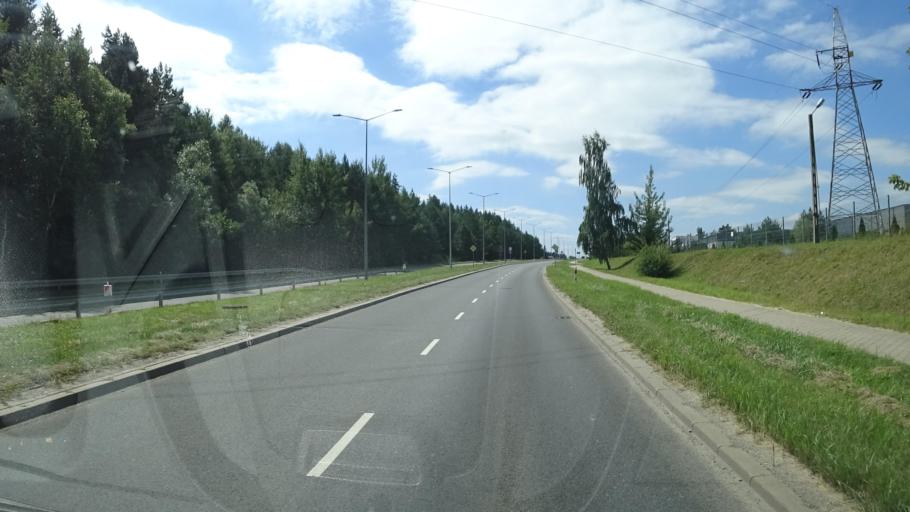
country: PL
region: Warmian-Masurian Voivodeship
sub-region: Powiat elcki
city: Elk
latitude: 53.8178
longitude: 22.3874
